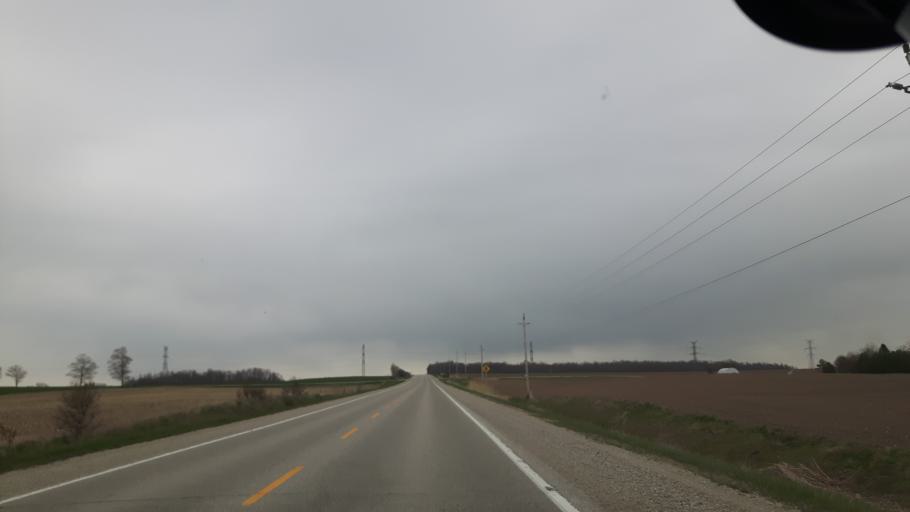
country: CA
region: Ontario
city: Bluewater
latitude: 43.5868
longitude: -81.6477
